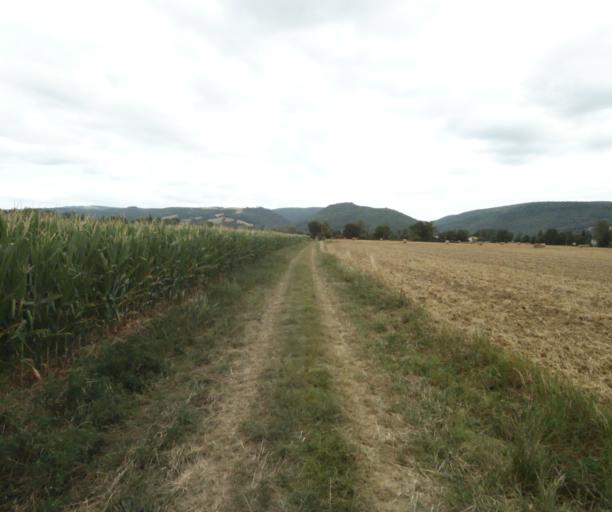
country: FR
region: Midi-Pyrenees
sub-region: Departement du Tarn
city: Soreze
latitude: 43.4610
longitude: 2.0468
